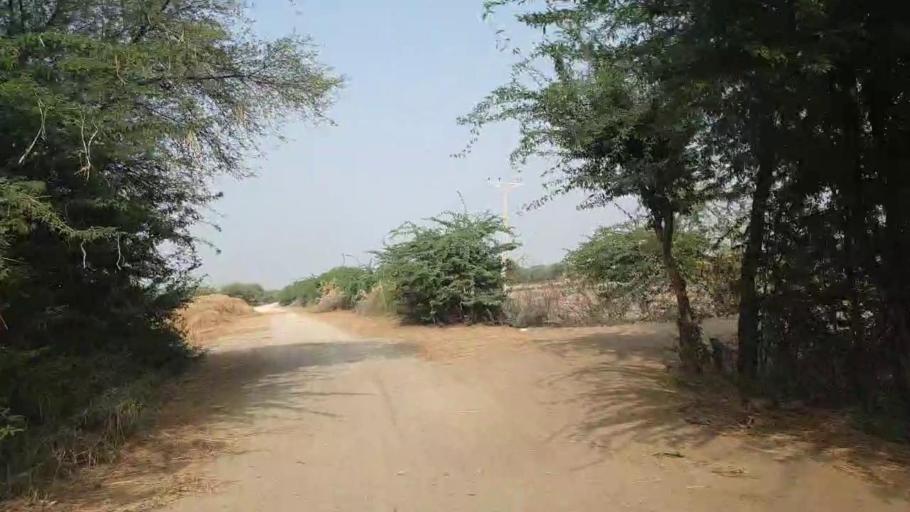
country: PK
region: Sindh
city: Kario
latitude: 24.9289
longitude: 68.6010
